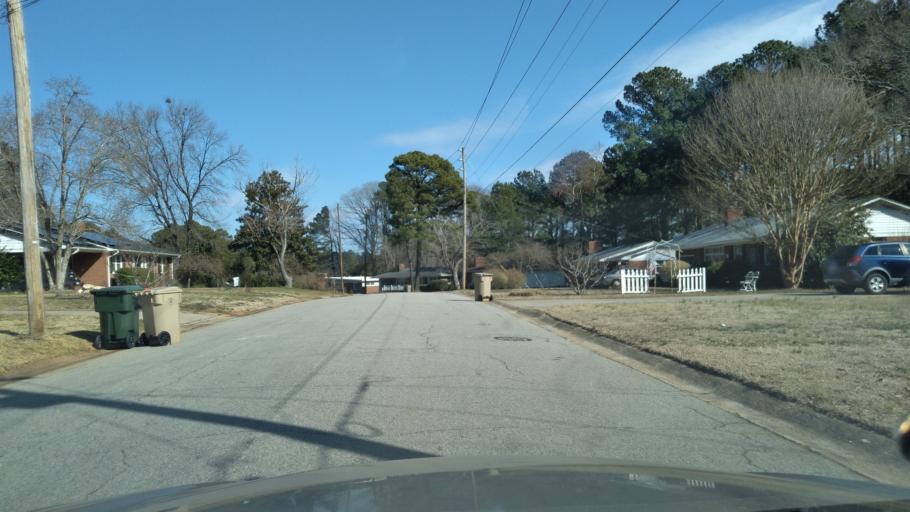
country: US
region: North Carolina
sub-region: Wake County
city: Garner
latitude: 35.6971
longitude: -78.6226
